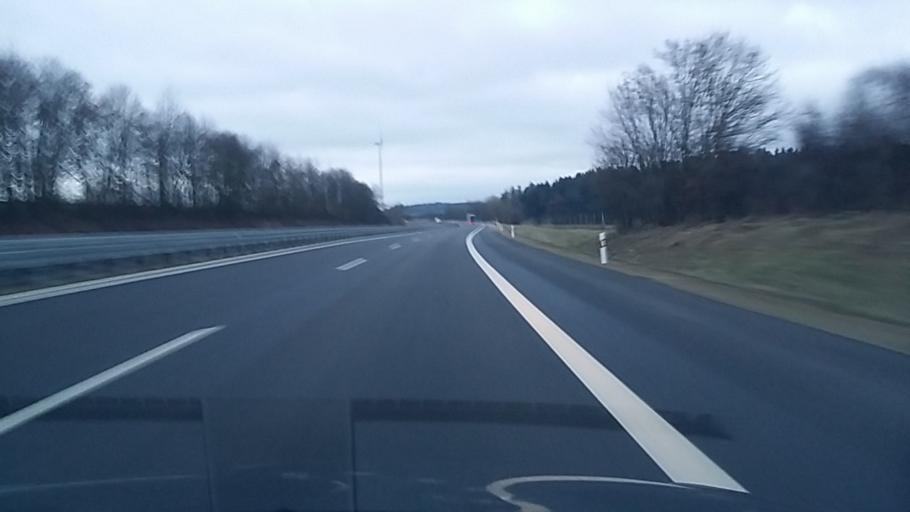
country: DE
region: Bavaria
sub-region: Upper Palatinate
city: Pilsach
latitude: 49.3020
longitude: 11.5503
